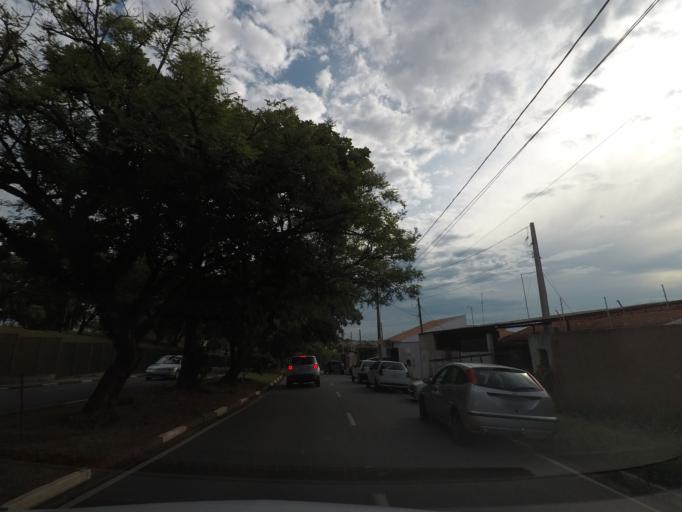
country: BR
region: Sao Paulo
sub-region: Campinas
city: Campinas
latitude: -22.9019
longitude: -47.1039
